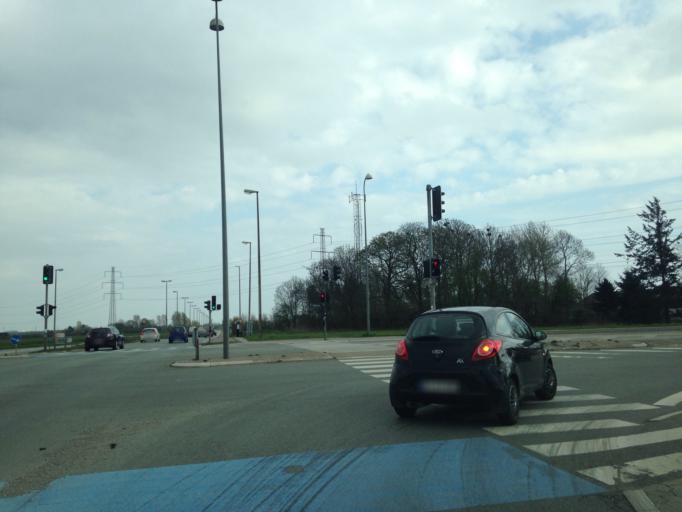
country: DK
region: Capital Region
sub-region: Hoje-Taastrup Kommune
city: Taastrup
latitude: 55.6341
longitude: 12.2868
